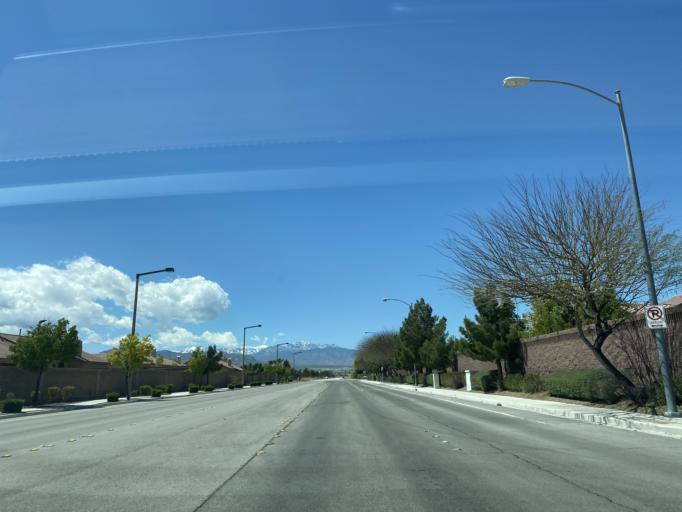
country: US
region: Nevada
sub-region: Clark County
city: North Las Vegas
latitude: 36.3127
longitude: -115.2288
